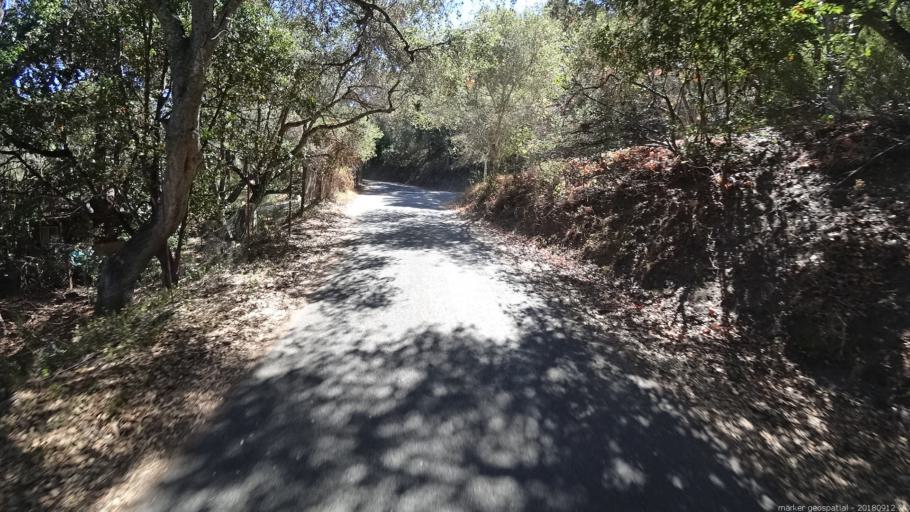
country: US
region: California
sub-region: Monterey County
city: Carmel Valley Village
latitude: 36.4690
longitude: -121.7326
